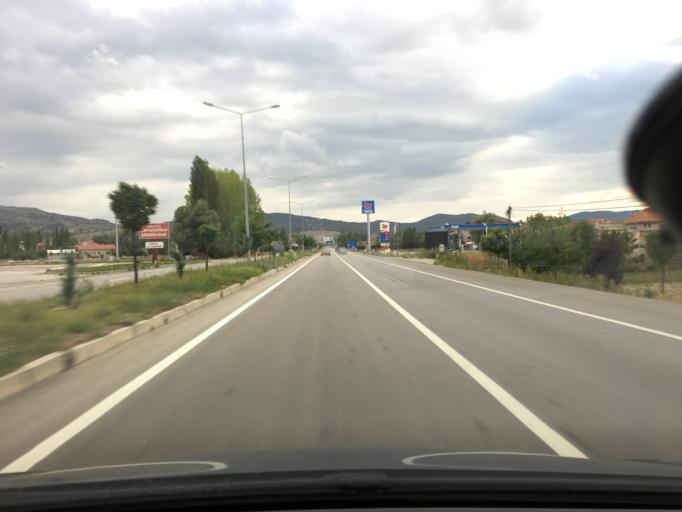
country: TR
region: Afyonkarahisar
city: Sincanli
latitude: 38.7384
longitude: 30.3507
